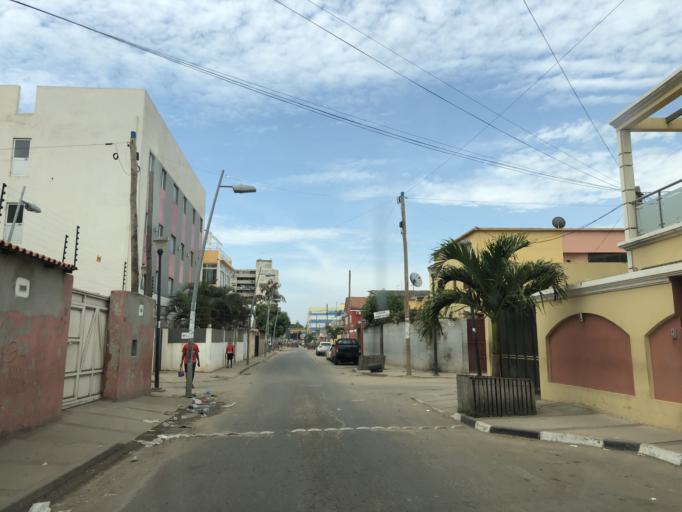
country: AO
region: Luanda
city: Luanda
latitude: -8.8220
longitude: 13.2517
